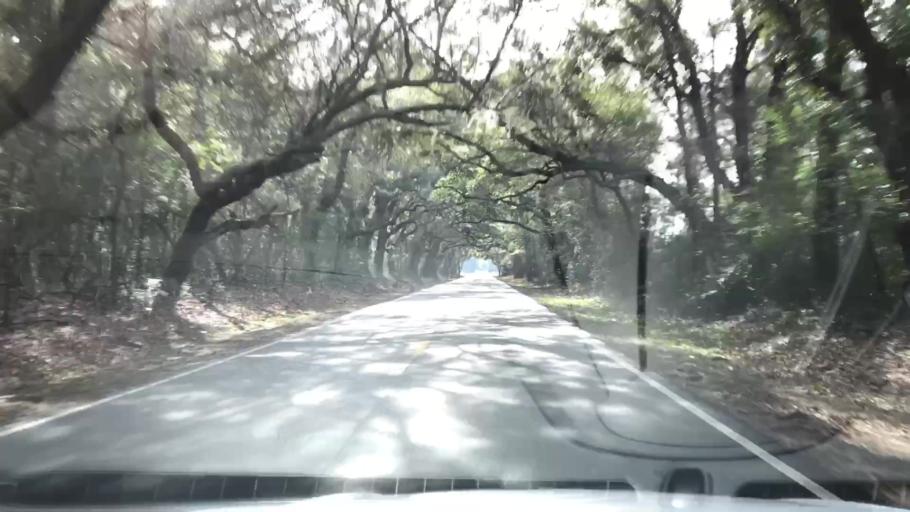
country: US
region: South Carolina
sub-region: Charleston County
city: Folly Beach
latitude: 32.7088
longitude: -80.0174
